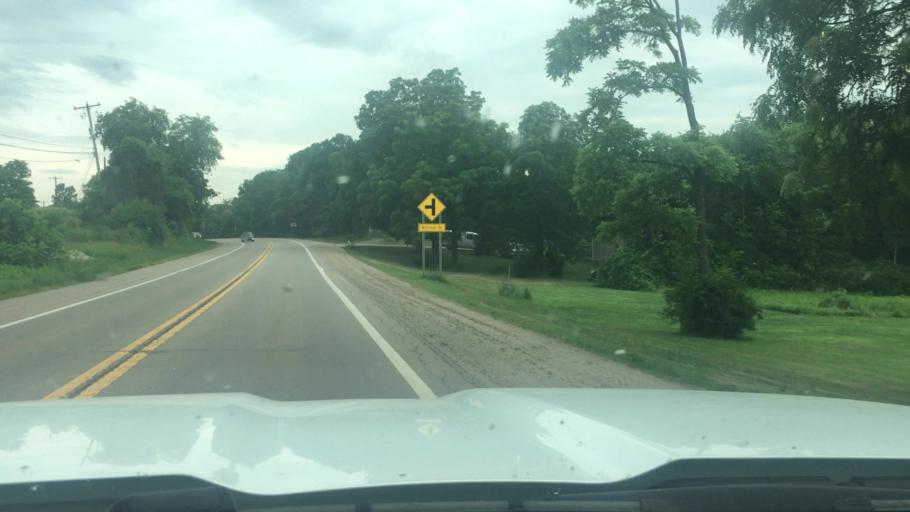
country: US
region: Michigan
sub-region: Ionia County
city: Ionia
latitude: 43.0019
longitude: -85.0128
